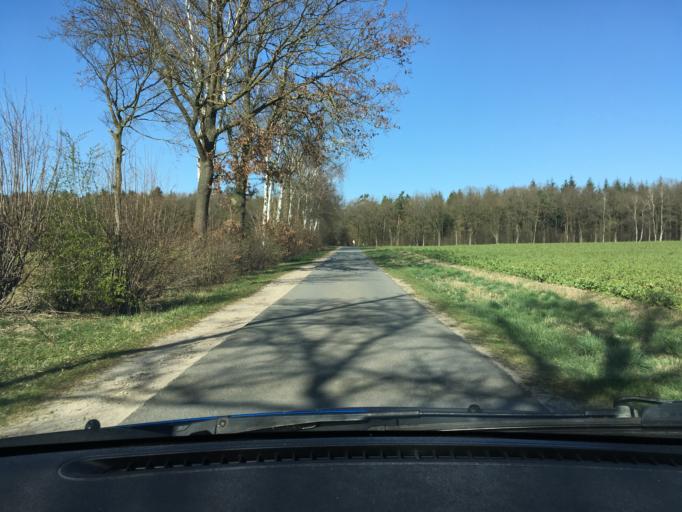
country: DE
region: Lower Saxony
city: Schwienau
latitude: 53.0286
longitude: 10.4444
